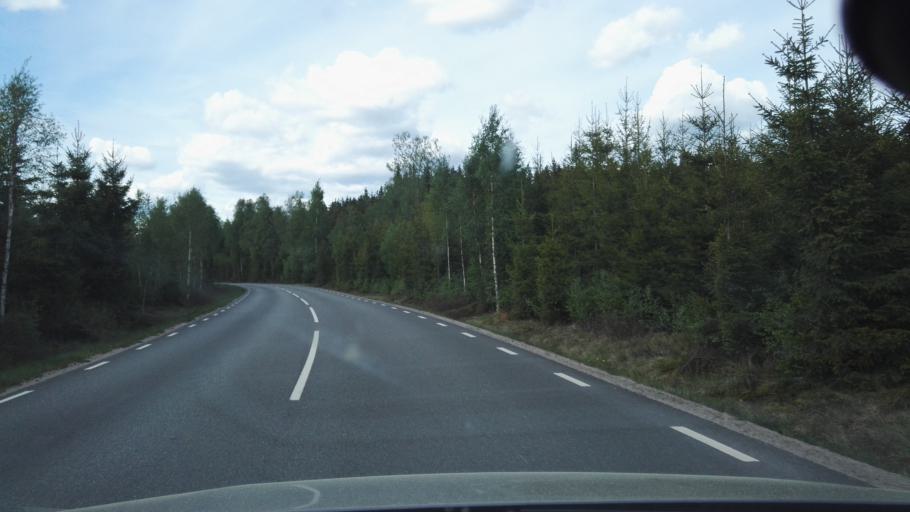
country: SE
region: Kronoberg
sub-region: Vaxjo Kommun
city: Braas
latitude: 57.1723
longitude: 14.9644
